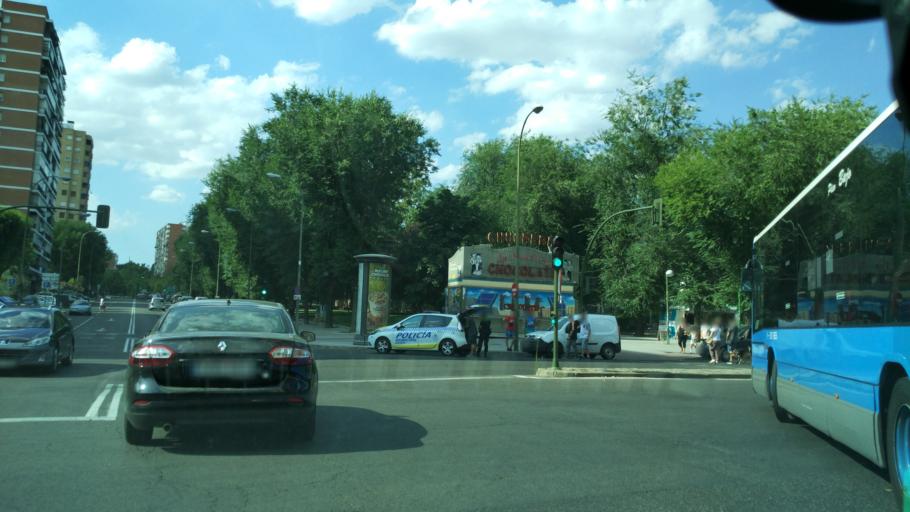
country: ES
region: Madrid
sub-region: Provincia de Madrid
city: Tetuan de las Victorias
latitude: 40.4775
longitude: -3.7120
